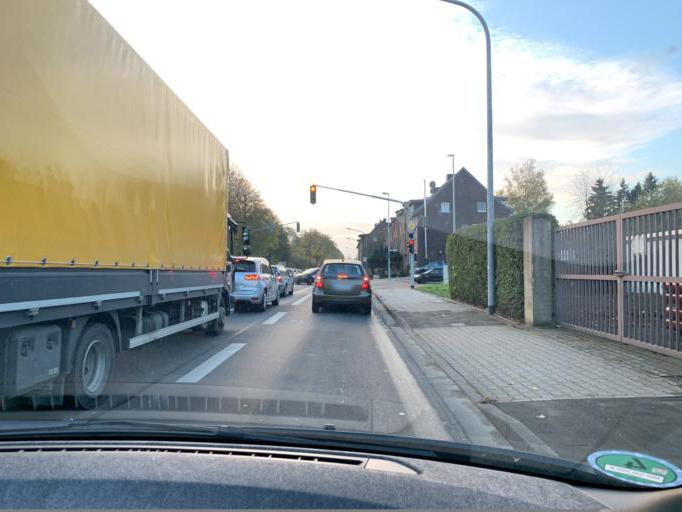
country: DE
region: North Rhine-Westphalia
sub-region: Regierungsbezirk Dusseldorf
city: Monchengladbach
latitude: 51.1474
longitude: 6.4501
